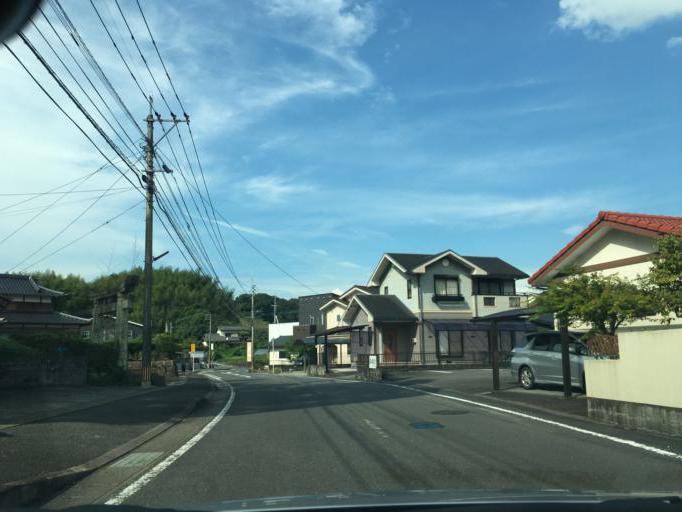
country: JP
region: Saga Prefecture
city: Takeocho-takeo
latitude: 33.1883
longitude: 130.0325
